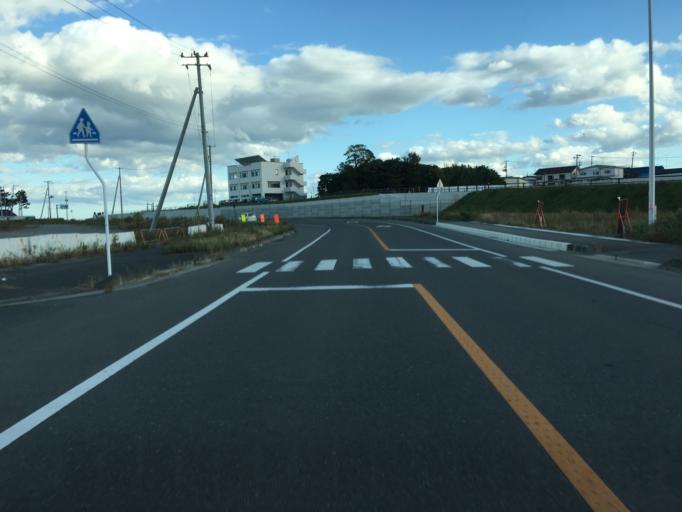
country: JP
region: Miyagi
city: Marumori
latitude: 37.8303
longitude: 140.9609
